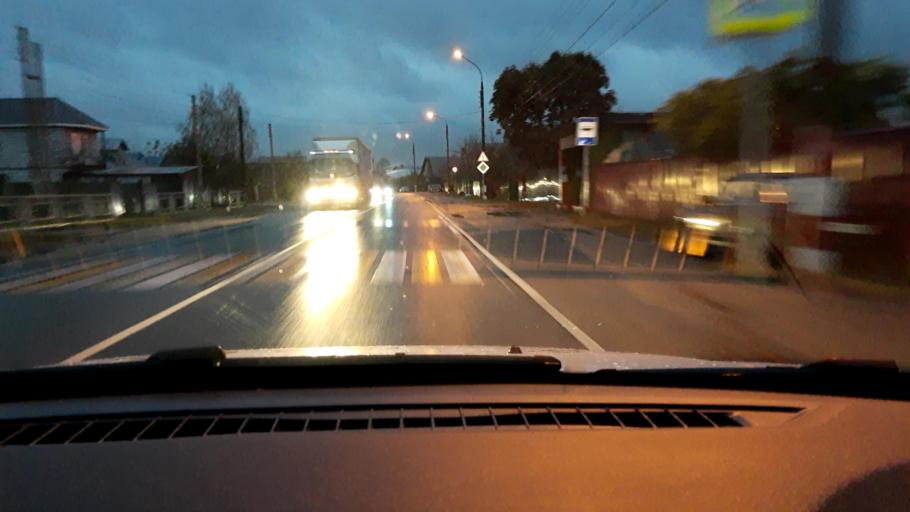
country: RU
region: Nizjnij Novgorod
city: Neklyudovo
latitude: 56.3819
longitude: 44.0143
